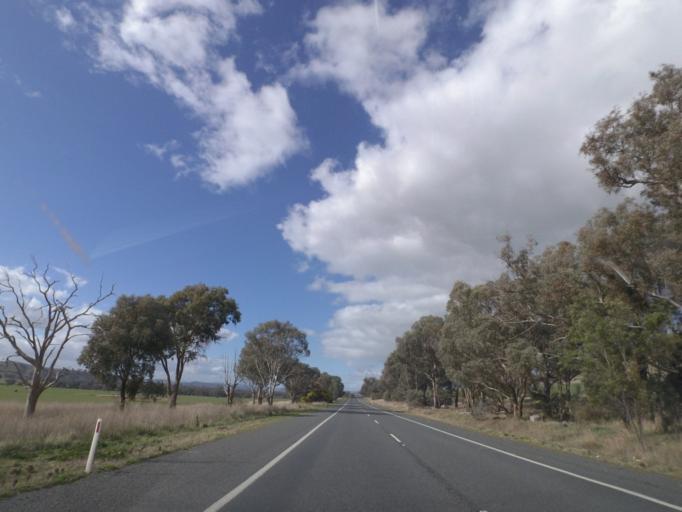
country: AU
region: New South Wales
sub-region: Greater Hume Shire
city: Holbrook
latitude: -35.6730
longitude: 147.3970
